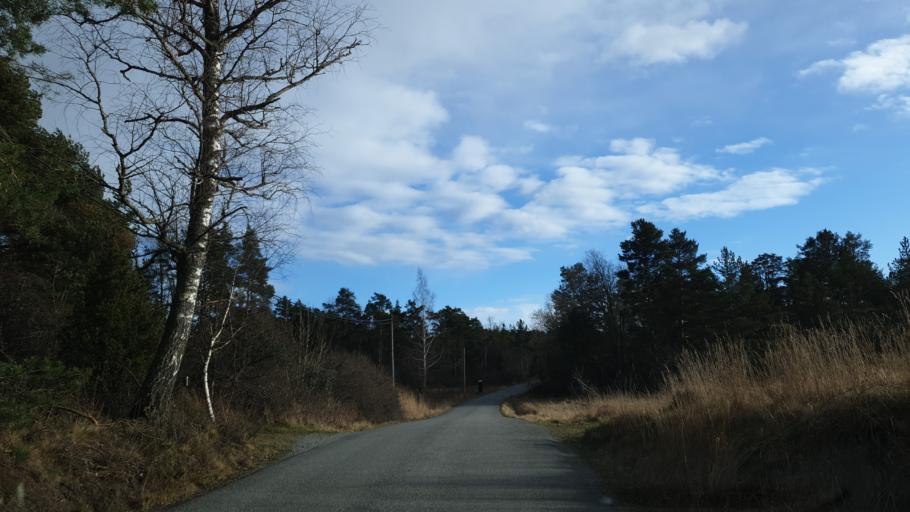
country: SE
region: Stockholm
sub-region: Varmdo Kommun
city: Holo
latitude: 59.3668
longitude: 18.6709
